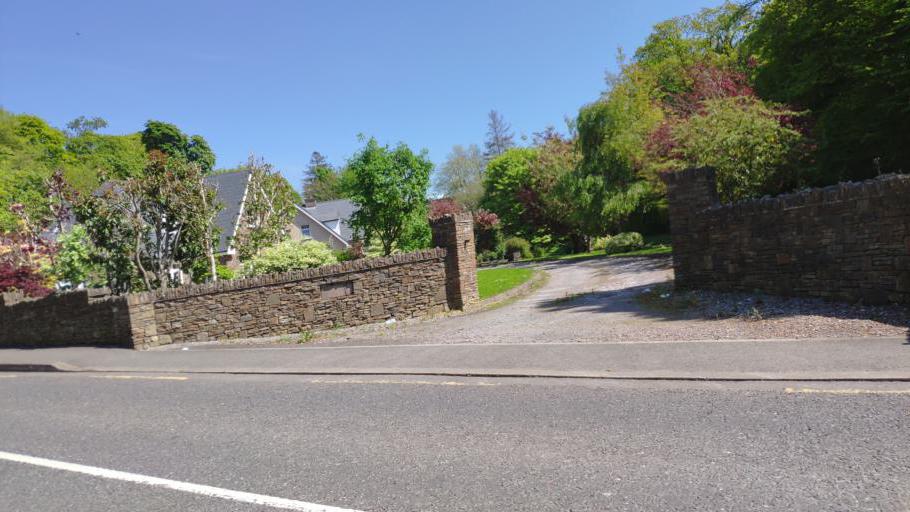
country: IE
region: Munster
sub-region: County Cork
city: Cork
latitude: 51.9250
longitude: -8.4911
